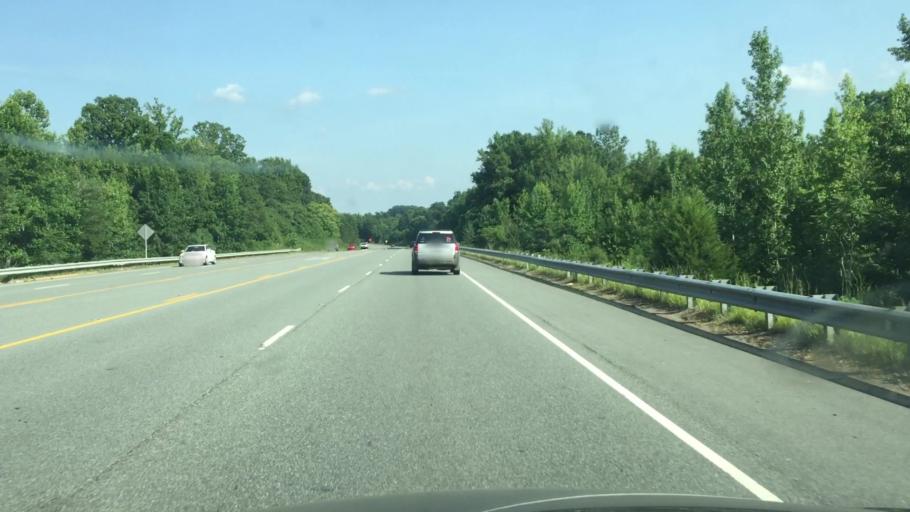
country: US
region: North Carolina
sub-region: Rockingham County
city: Reidsville
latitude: 36.3678
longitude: -79.6437
